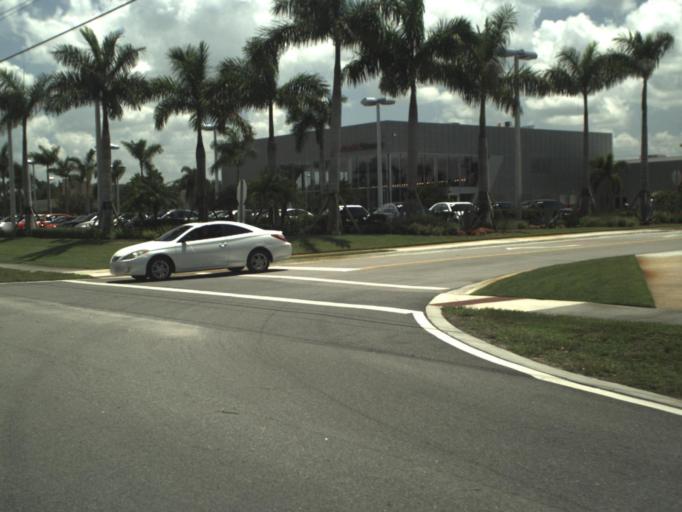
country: US
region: Florida
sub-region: Martin County
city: Port Salerno
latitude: 27.1570
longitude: -80.2216
